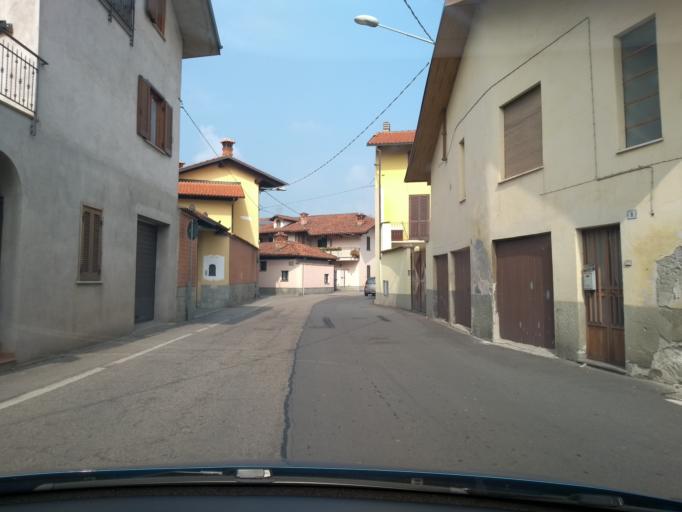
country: IT
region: Piedmont
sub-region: Provincia di Torino
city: Favria
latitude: 45.3331
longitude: 7.6895
